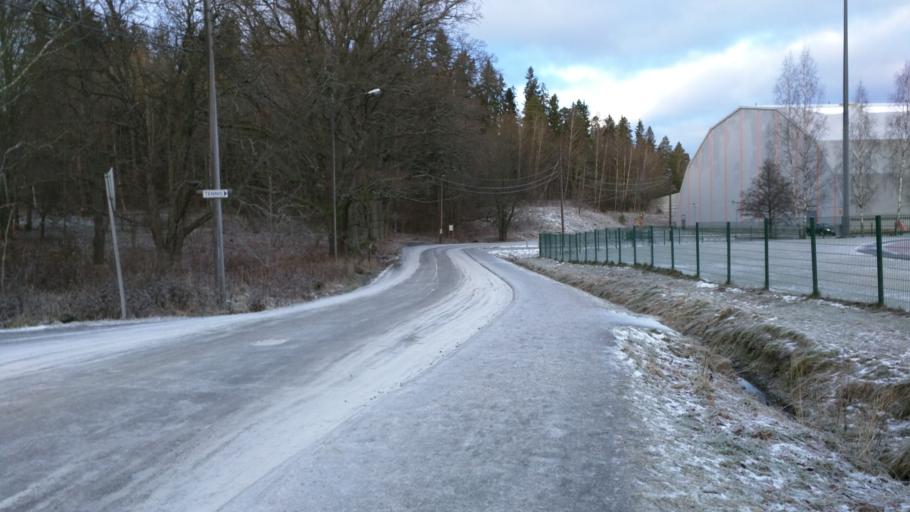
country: FI
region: Uusimaa
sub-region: Helsinki
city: Kauniainen
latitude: 60.2444
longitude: 24.7463
